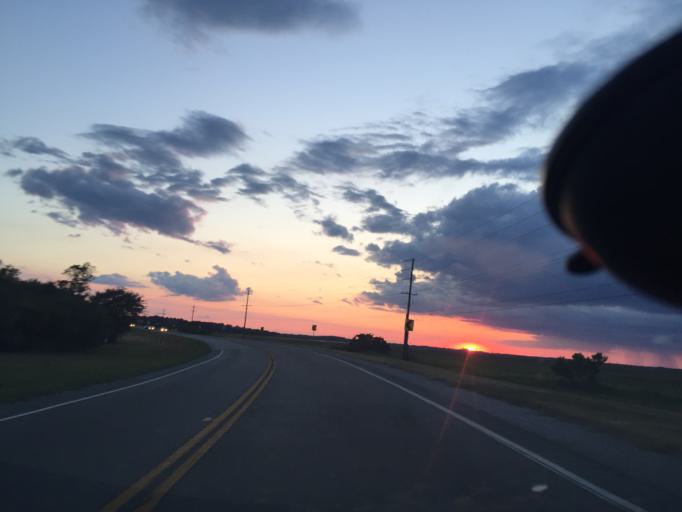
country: US
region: Georgia
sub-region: Chatham County
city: Wilmington Island
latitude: 32.0410
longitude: -80.9476
